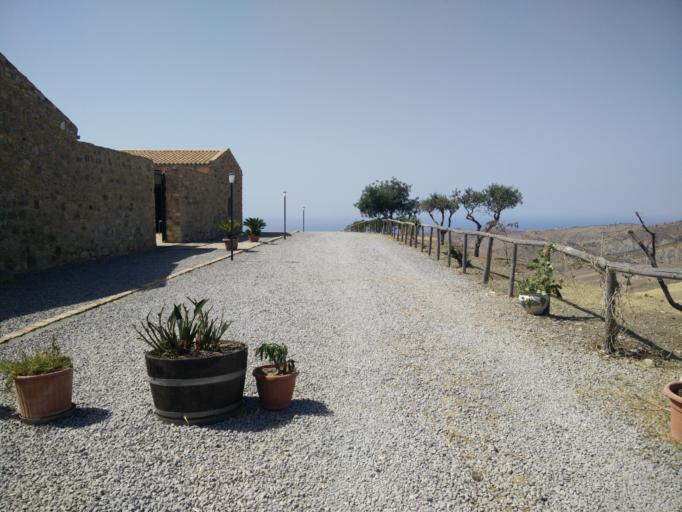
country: IT
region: Sicily
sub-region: Palermo
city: Cerda
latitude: 37.9280
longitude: 13.8739
